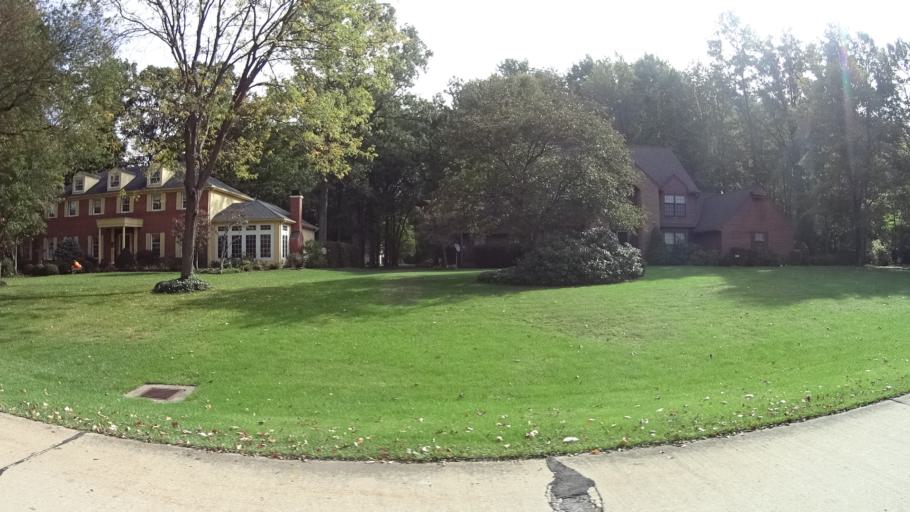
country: US
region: Ohio
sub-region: Lorain County
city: Grafton
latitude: 41.3263
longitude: -82.0653
